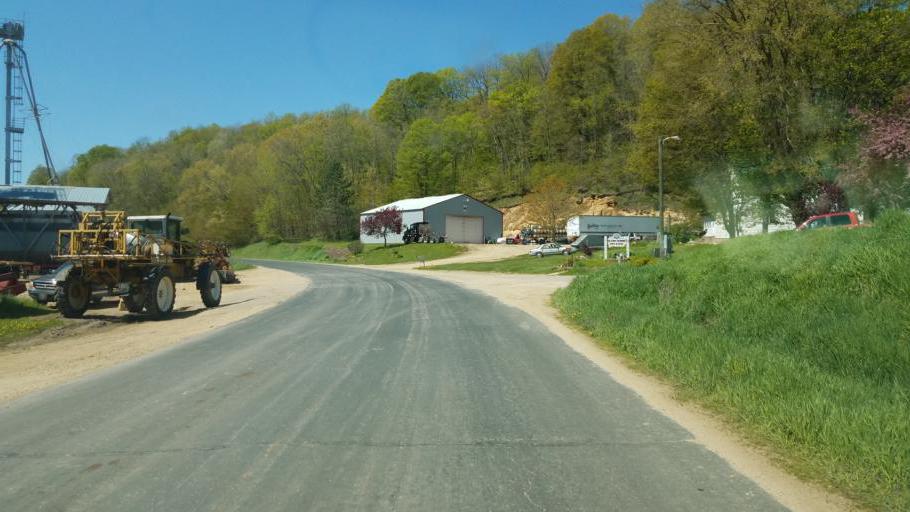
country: US
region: Wisconsin
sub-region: Vernon County
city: Hillsboro
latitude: 43.5752
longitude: -90.3806
